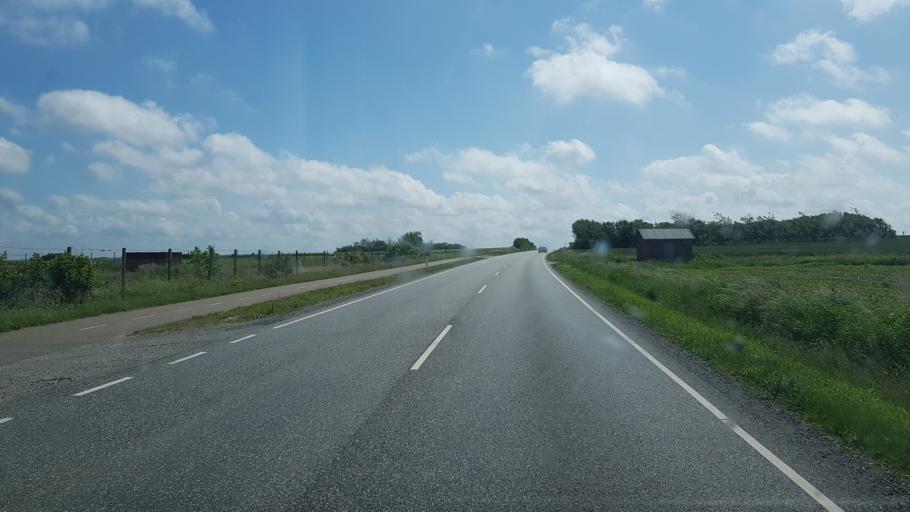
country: DK
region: Central Jutland
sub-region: Lemvig Kommune
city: Lemvig
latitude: 56.5528
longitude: 8.2494
